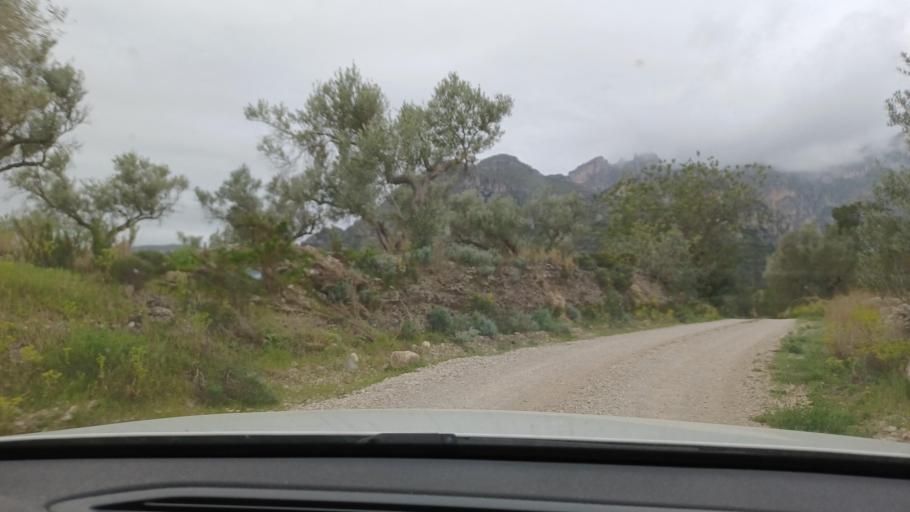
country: ES
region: Catalonia
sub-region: Provincia de Tarragona
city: Mas de Barberans
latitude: 40.8054
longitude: 0.4066
